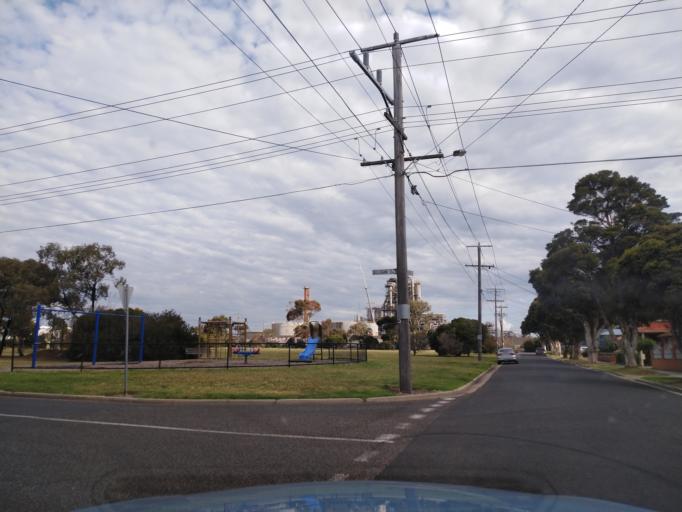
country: AU
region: Victoria
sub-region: Hobsons Bay
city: Altona North
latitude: -37.8455
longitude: 144.8520
